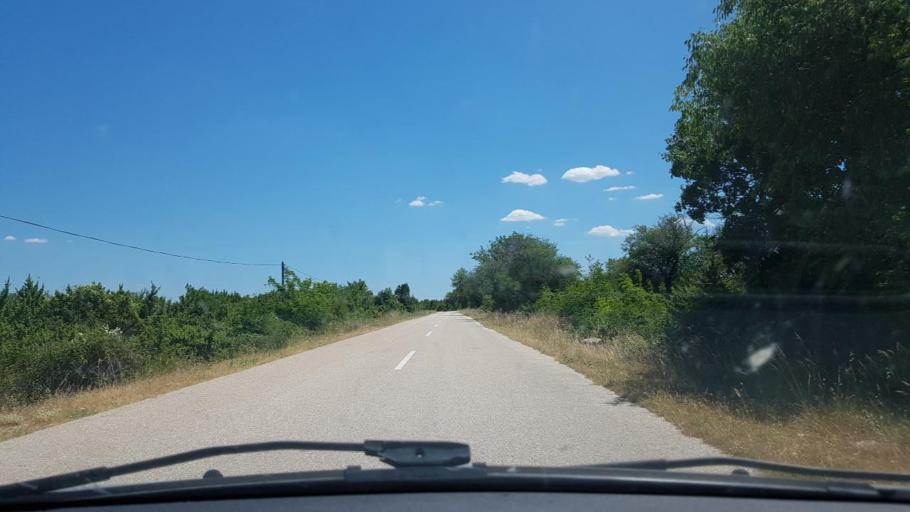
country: HR
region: Sibensko-Kniniska
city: Kistanje
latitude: 43.9715
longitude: 15.9735
